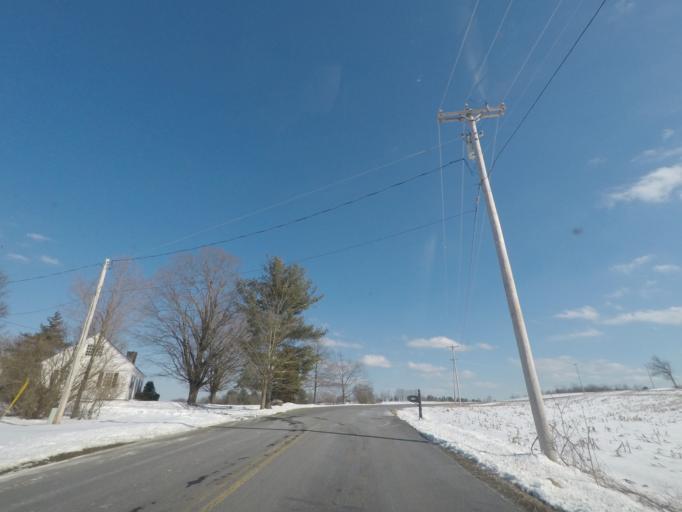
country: US
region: New York
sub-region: Rensselaer County
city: Hoosick Falls
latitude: 42.8705
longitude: -73.4932
